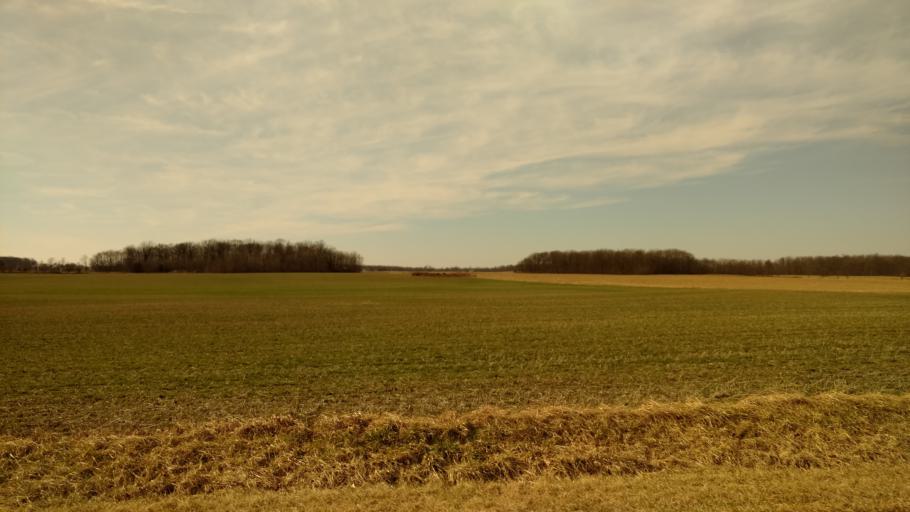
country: US
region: Ohio
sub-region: Hardin County
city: Kenton
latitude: 40.5865
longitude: -83.5051
